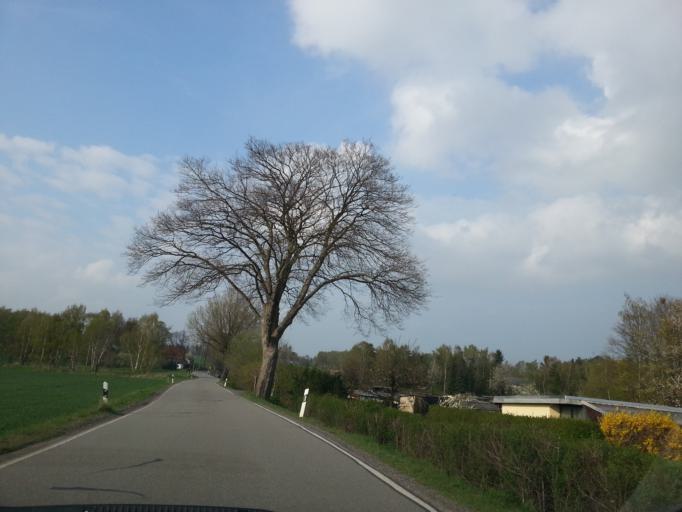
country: DE
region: Saxony
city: Brand-Erbisdorf
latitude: 50.8749
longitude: 13.3356
